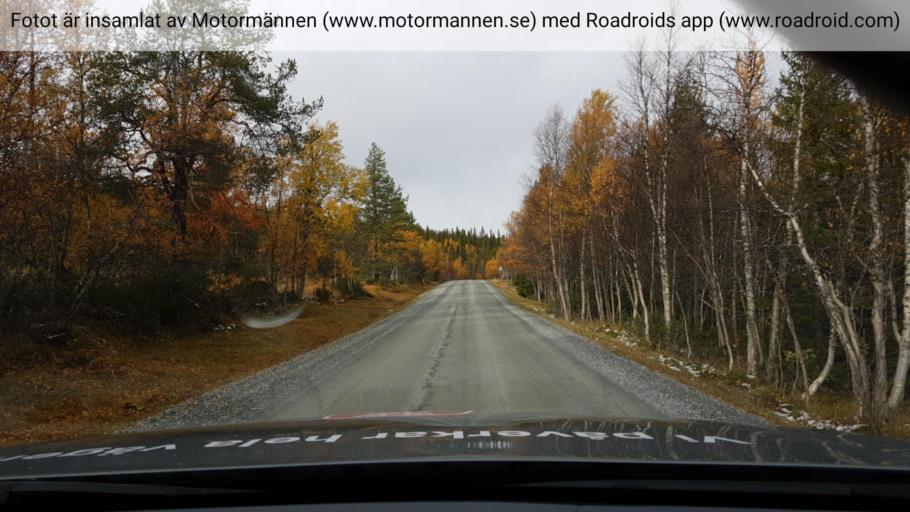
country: SE
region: Jaemtland
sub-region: Are Kommun
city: Are
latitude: 62.7931
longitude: 12.7643
